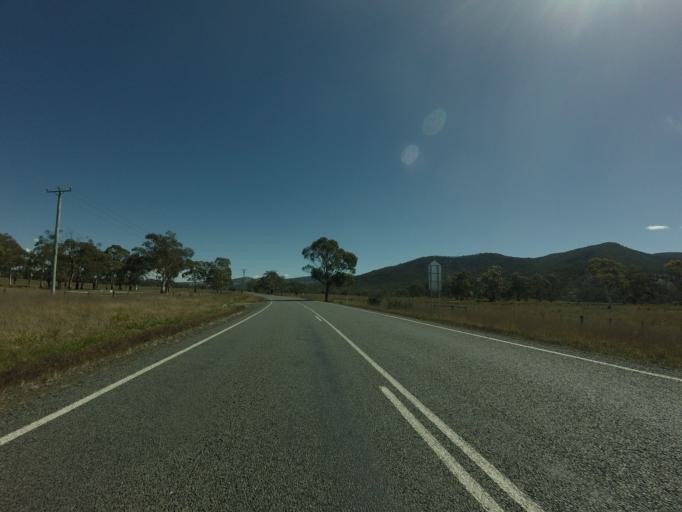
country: AU
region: Tasmania
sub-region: Northern Midlands
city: Evandale
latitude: -41.7522
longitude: 147.7696
